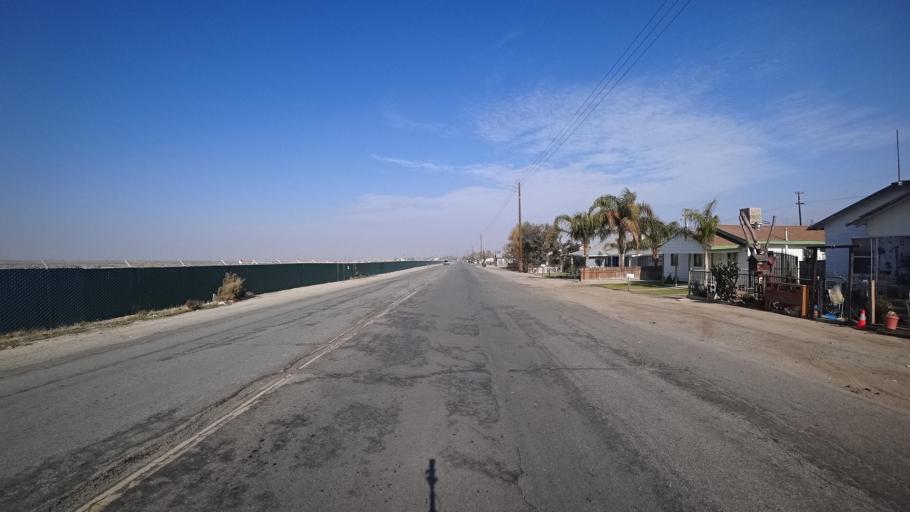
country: US
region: California
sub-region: Kern County
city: Ford City
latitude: 35.1595
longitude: -119.4652
